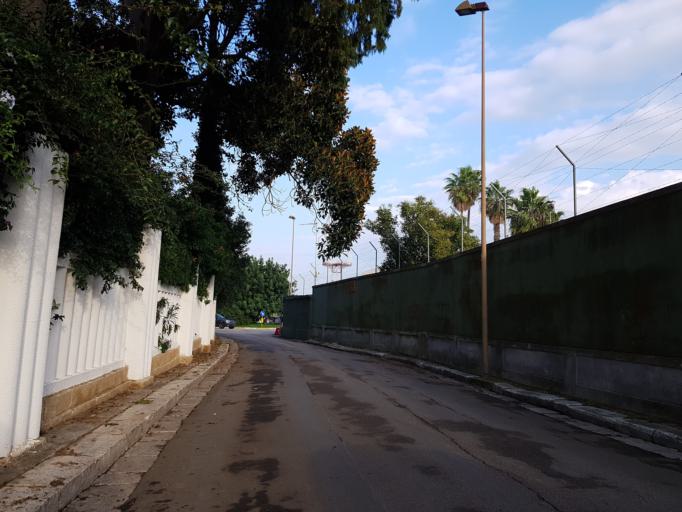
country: IT
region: Apulia
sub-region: Provincia di Brindisi
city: Materdomini
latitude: 40.6491
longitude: 17.9470
